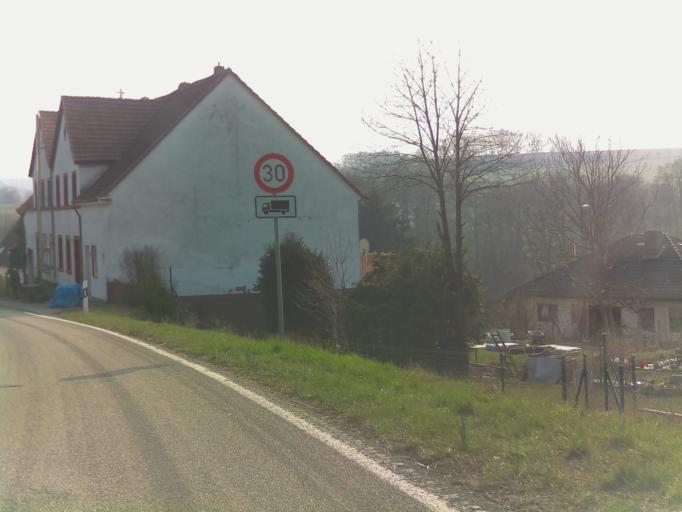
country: DE
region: Rheinland-Pfalz
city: Thallichtenberg
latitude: 49.5610
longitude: 7.3485
